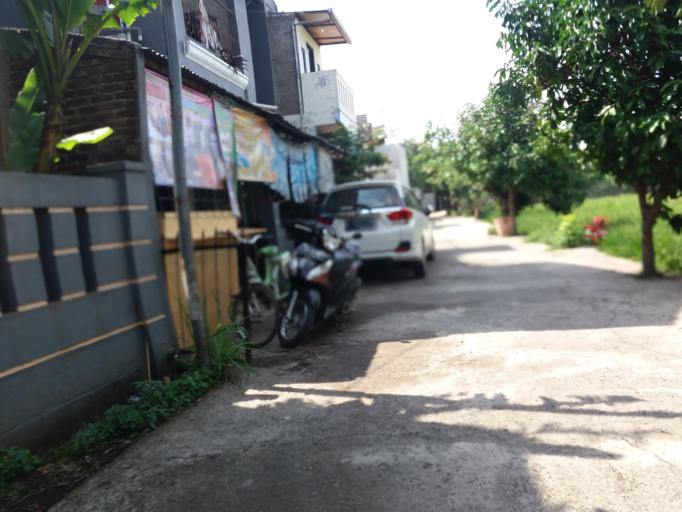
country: ID
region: West Java
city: Bandung
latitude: -6.9208
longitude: 107.6640
